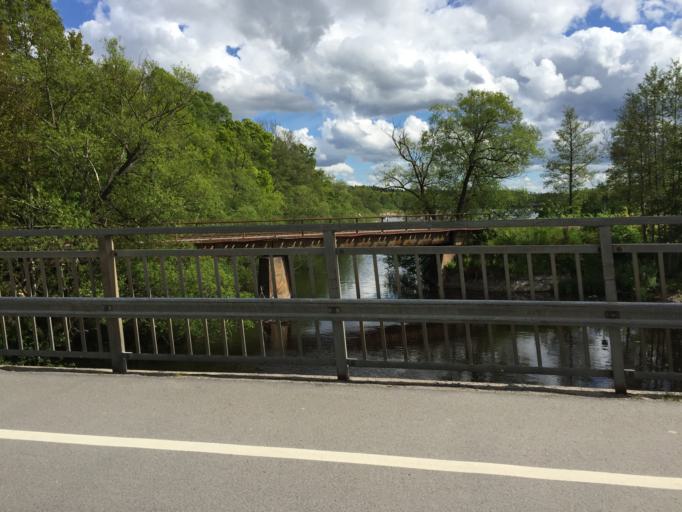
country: SE
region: OEstergoetland
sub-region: Finspangs Kommun
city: Finspang
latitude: 58.7088
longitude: 15.7780
